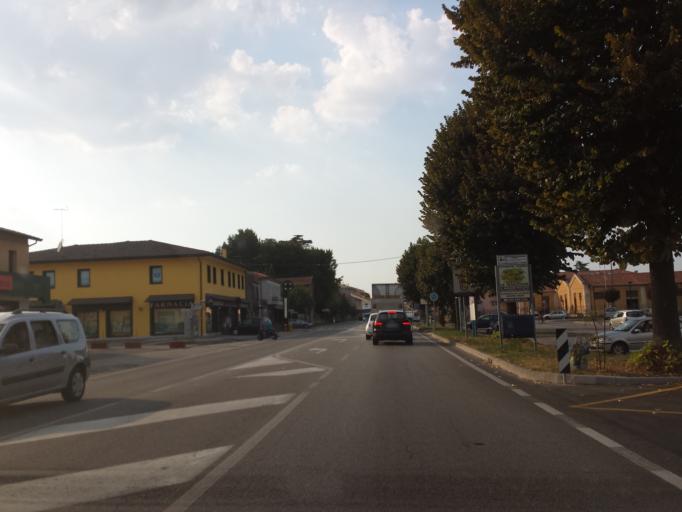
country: IT
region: Veneto
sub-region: Provincia di Padova
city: Mestrino
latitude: 45.4405
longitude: 11.7620
